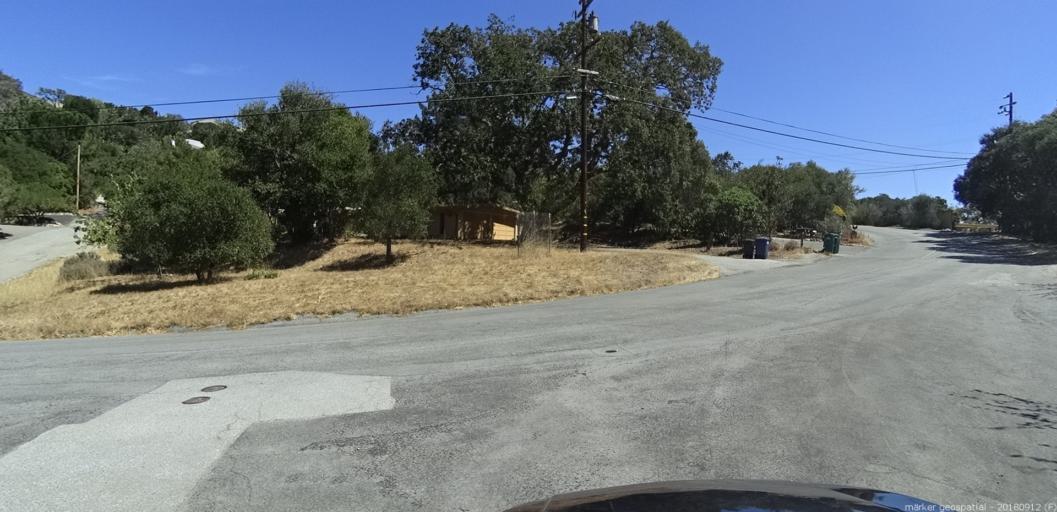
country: US
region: California
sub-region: Monterey County
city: Carmel Valley Village
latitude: 36.4909
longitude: -121.7426
